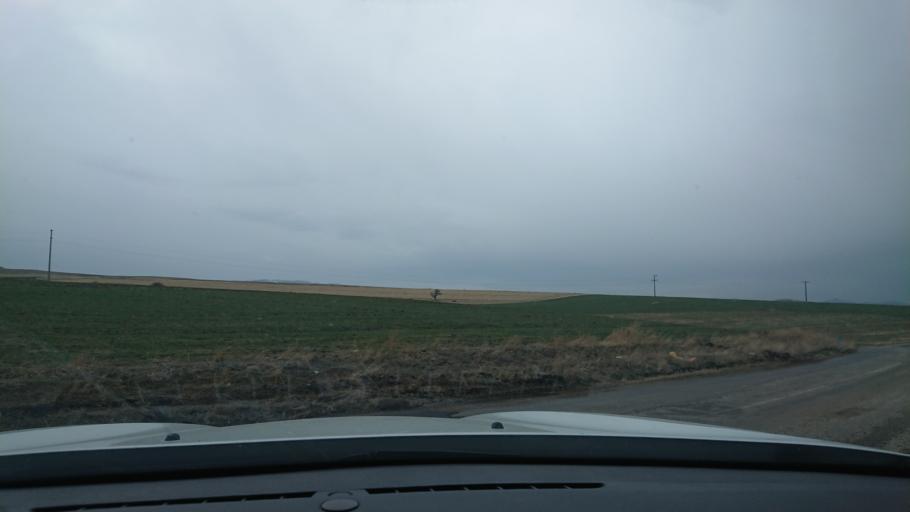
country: TR
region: Aksaray
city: Agacoren
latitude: 38.9438
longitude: 33.9108
